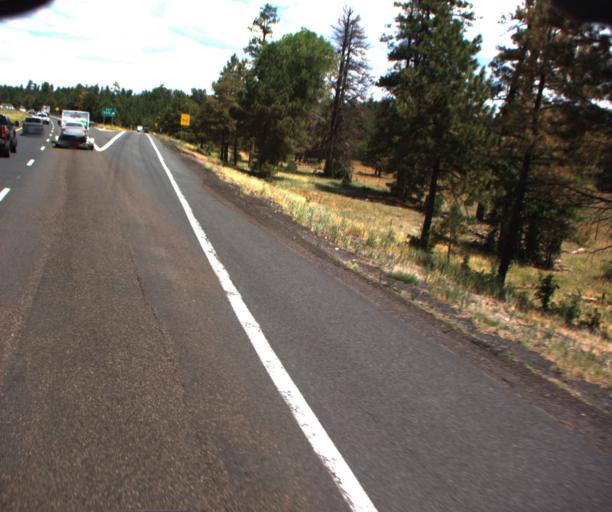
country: US
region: Arizona
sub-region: Coconino County
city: Sedona
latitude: 34.9092
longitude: -111.6410
